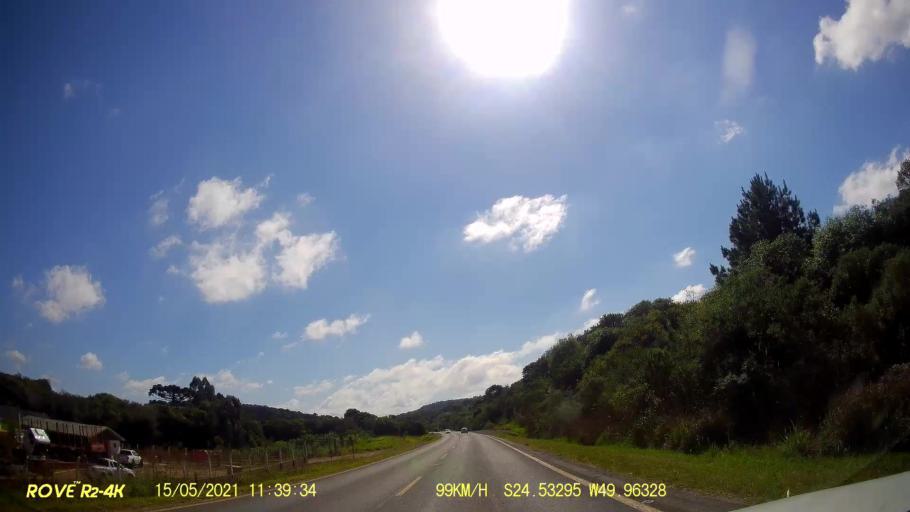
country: BR
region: Parana
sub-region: Pirai Do Sul
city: Pirai do Sul
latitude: -24.5331
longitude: -49.9633
